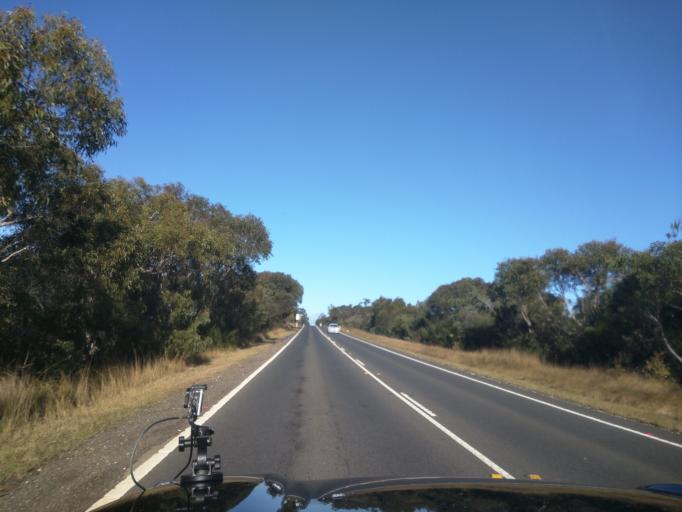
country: AU
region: New South Wales
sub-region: Sutherland Shire
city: Menai
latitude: -34.0091
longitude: 150.9886
